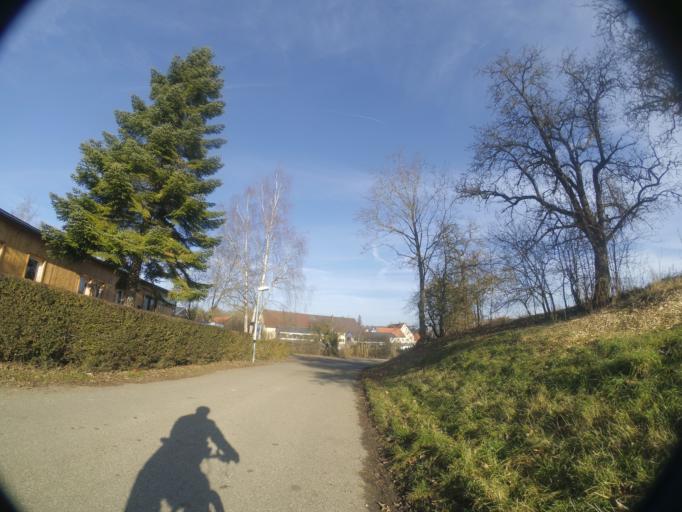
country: DE
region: Baden-Wuerttemberg
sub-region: Tuebingen Region
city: Dornstadt
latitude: 48.4634
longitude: 9.9401
